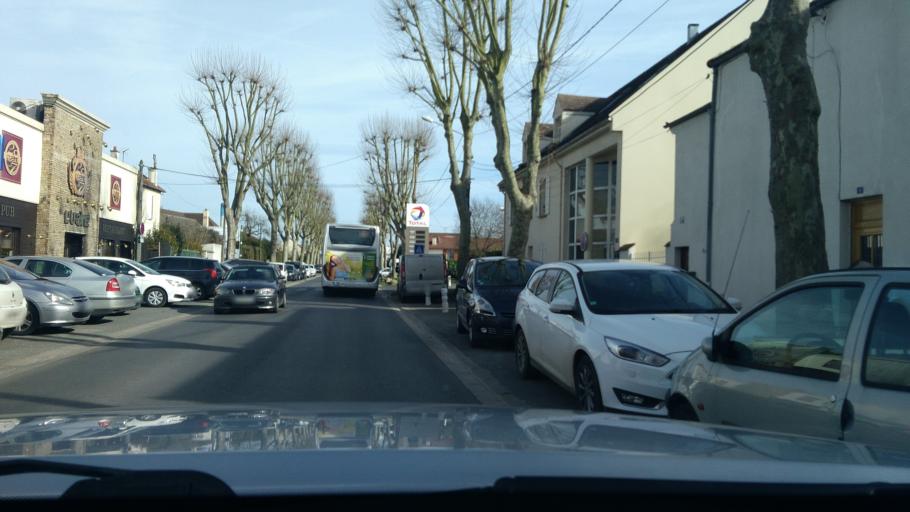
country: FR
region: Ile-de-France
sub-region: Departement de Seine-et-Marne
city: Melun
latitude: 48.5411
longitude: 2.6746
